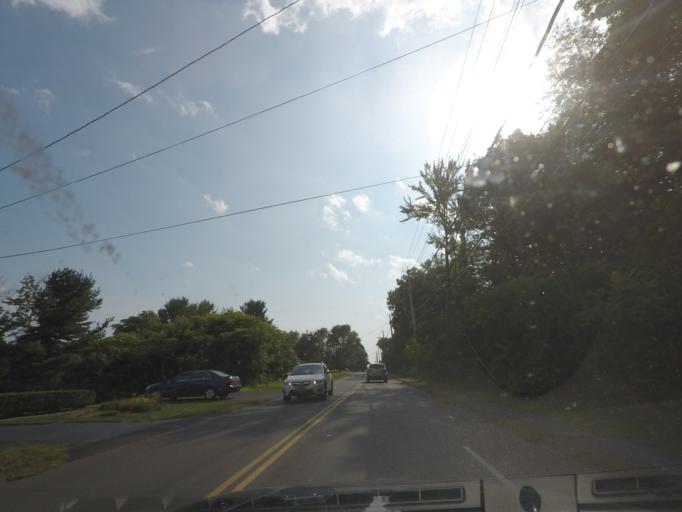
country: US
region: New York
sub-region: Rensselaer County
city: Troy
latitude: 42.7339
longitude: -73.6604
